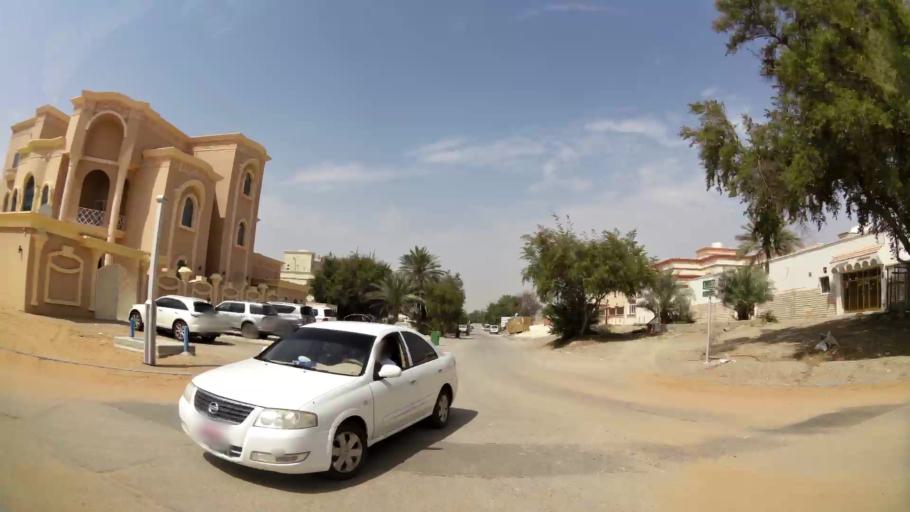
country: AE
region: Abu Dhabi
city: Abu Dhabi
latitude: 24.2992
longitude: 54.6303
